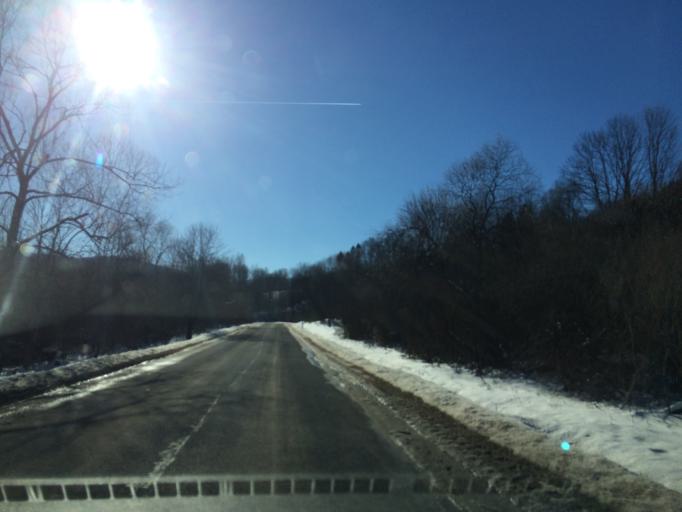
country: PL
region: Subcarpathian Voivodeship
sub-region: Powiat bieszczadzki
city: Lutowiska
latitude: 49.1744
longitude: 22.6861
